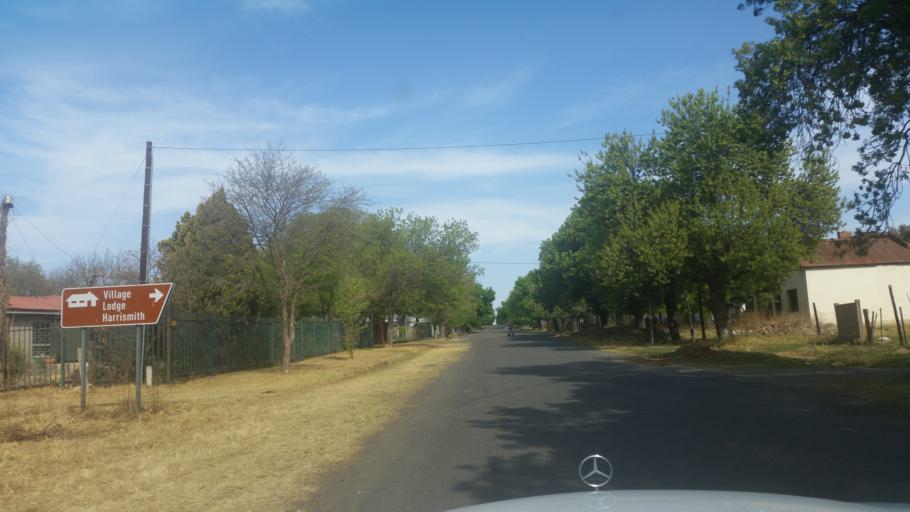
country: ZA
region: Orange Free State
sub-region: Thabo Mofutsanyana District Municipality
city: Harrismith
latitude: -28.2626
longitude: 29.1199
